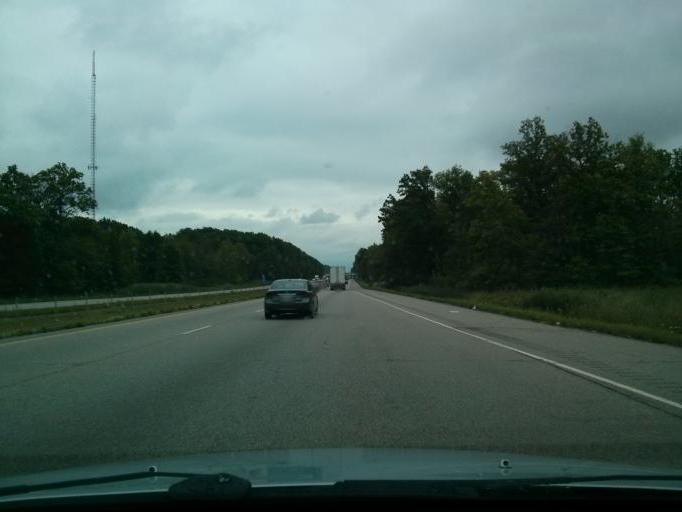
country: US
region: Ohio
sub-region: Portage County
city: Brimfield
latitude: 41.1076
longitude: -81.3409
